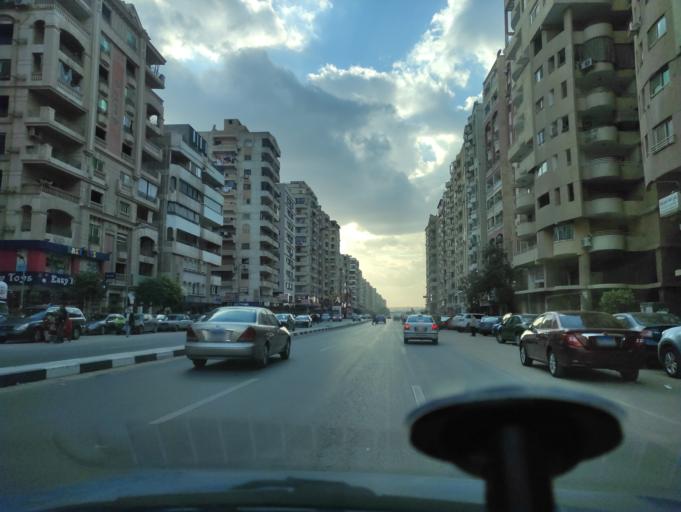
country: EG
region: Muhafazat al Qalyubiyah
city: Al Khankah
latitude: 30.1295
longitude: 31.3761
